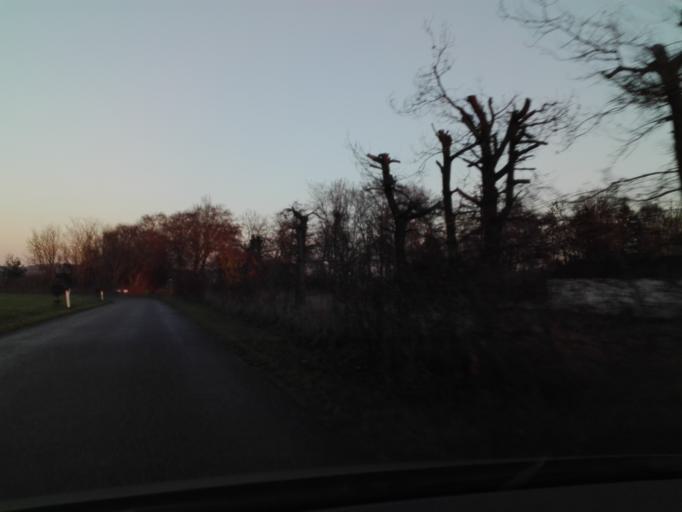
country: DK
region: Central Jutland
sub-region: Arhus Kommune
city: Kolt
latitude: 56.1383
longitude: 10.0501
